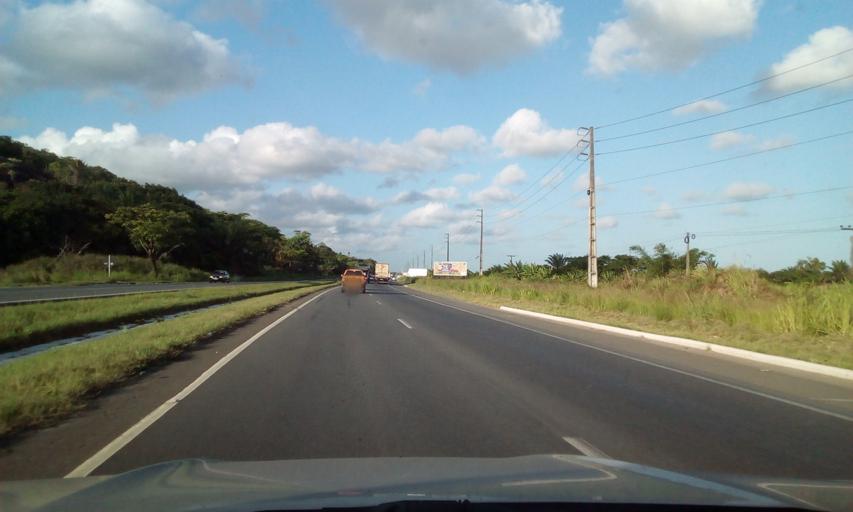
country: BR
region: Pernambuco
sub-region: Jaboatao Dos Guararapes
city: Jaboatao
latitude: -8.2092
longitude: -34.9848
